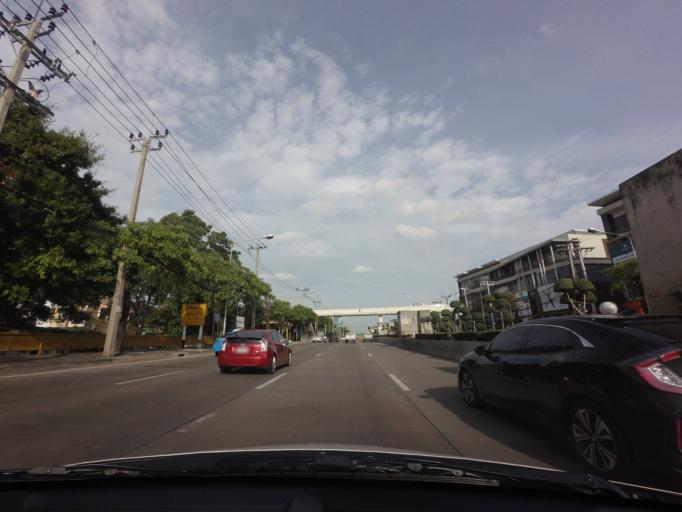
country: TH
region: Bangkok
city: Khan Na Yao
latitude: 13.8142
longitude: 100.6447
